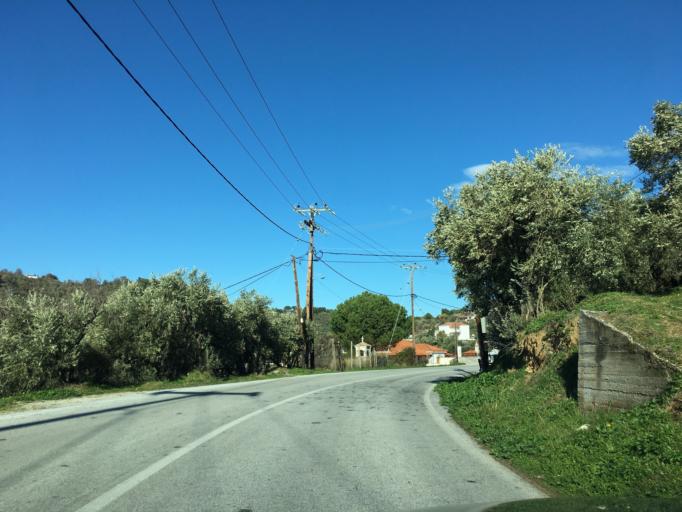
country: GR
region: Thessaly
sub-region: Nomos Magnisias
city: Skopelos
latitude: 39.1718
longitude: 23.6240
